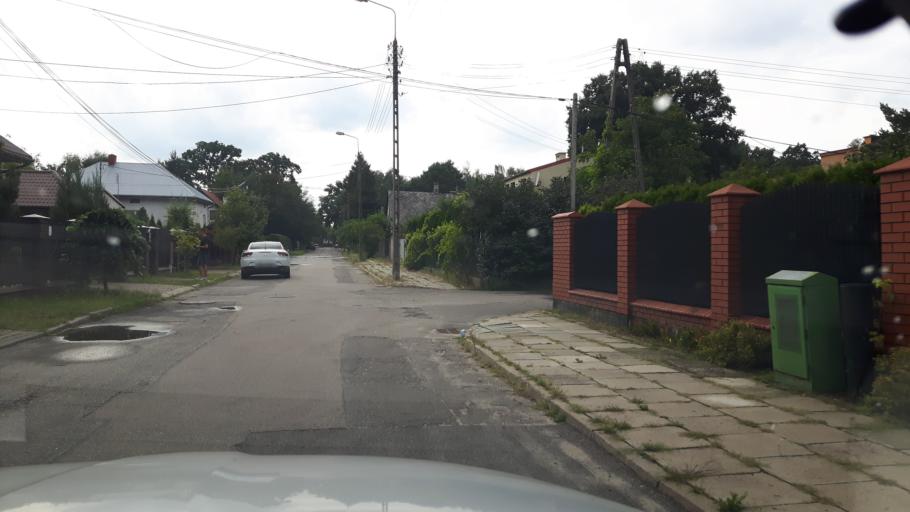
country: PL
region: Masovian Voivodeship
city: Zielonka
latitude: 52.3152
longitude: 21.1380
